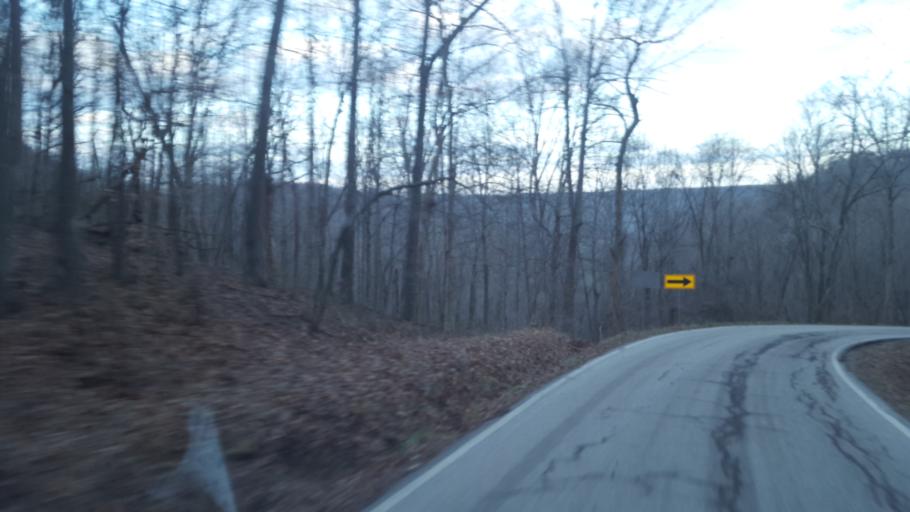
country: US
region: Ohio
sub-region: Adams County
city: Manchester
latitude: 38.5200
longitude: -83.5137
